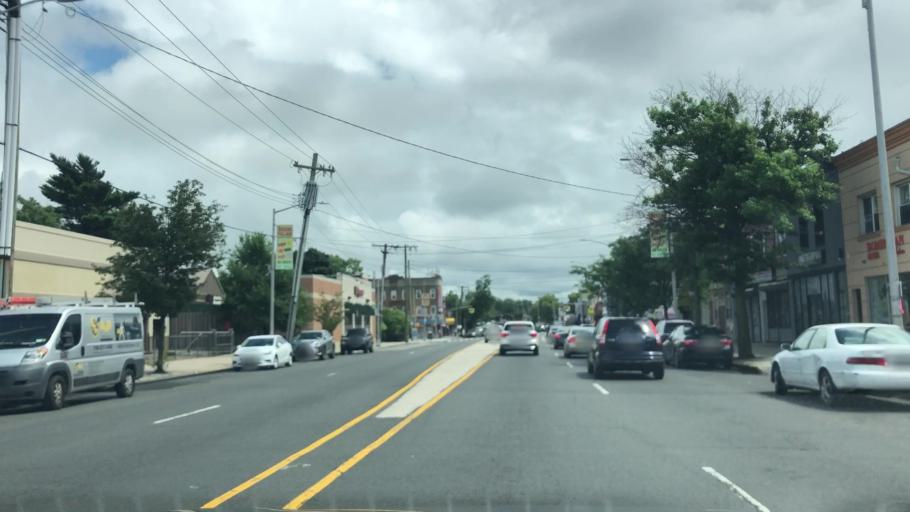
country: US
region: New York
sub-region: Nassau County
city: Bellerose Terrace
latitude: 40.7138
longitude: -73.7375
